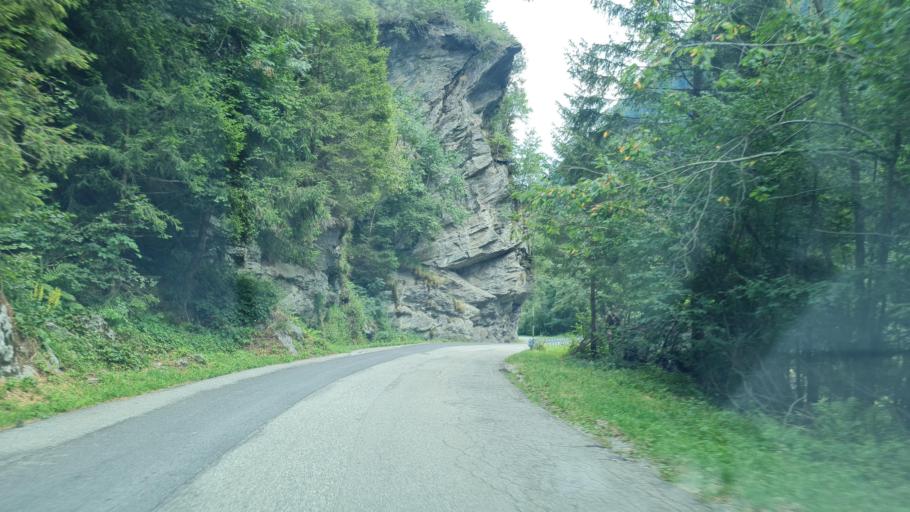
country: IT
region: Piedmont
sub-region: Provincia Verbano-Cusio-Ossola
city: Baceno
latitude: 46.2890
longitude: 8.2749
